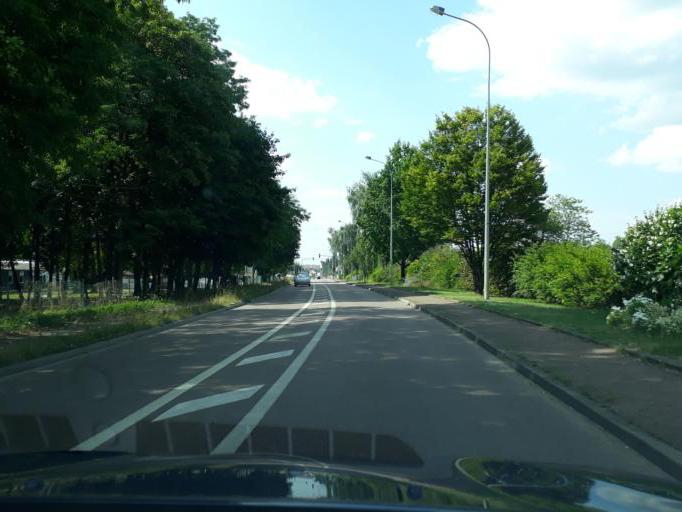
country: FR
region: Bourgogne
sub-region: Departement de la Nievre
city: Fourchambault
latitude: 47.0073
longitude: 3.0942
